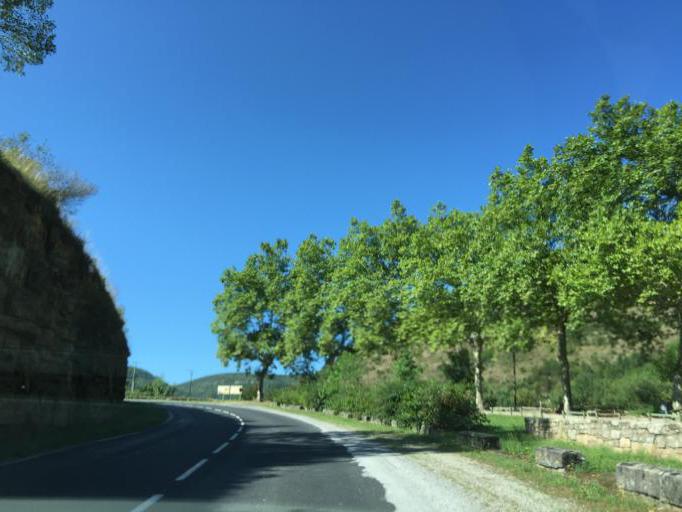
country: FR
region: Midi-Pyrenees
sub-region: Departement de l'Aveyron
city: Saint-Georges-de-Luzencon
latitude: 44.0571
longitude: 2.9020
